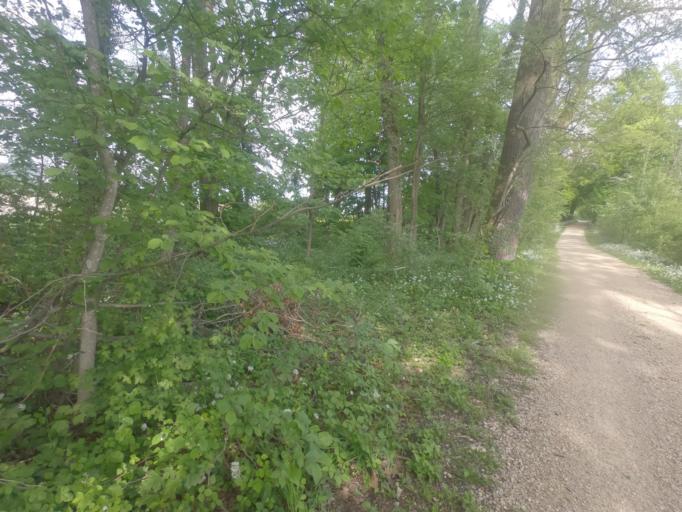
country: CH
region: Solothurn
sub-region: Bezirk Wasseramt
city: Deitingen
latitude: 47.2306
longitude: 7.6153
